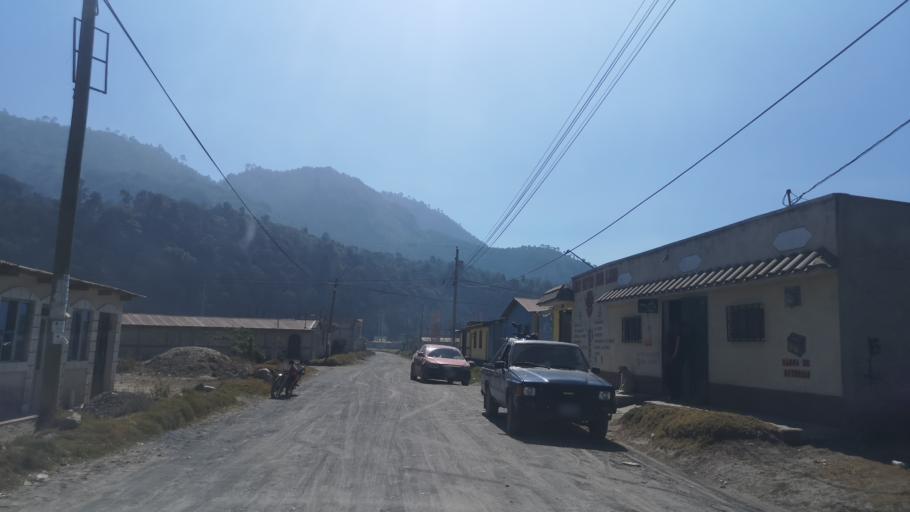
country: GT
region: Quetzaltenango
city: Almolonga
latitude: 14.7889
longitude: -91.5395
